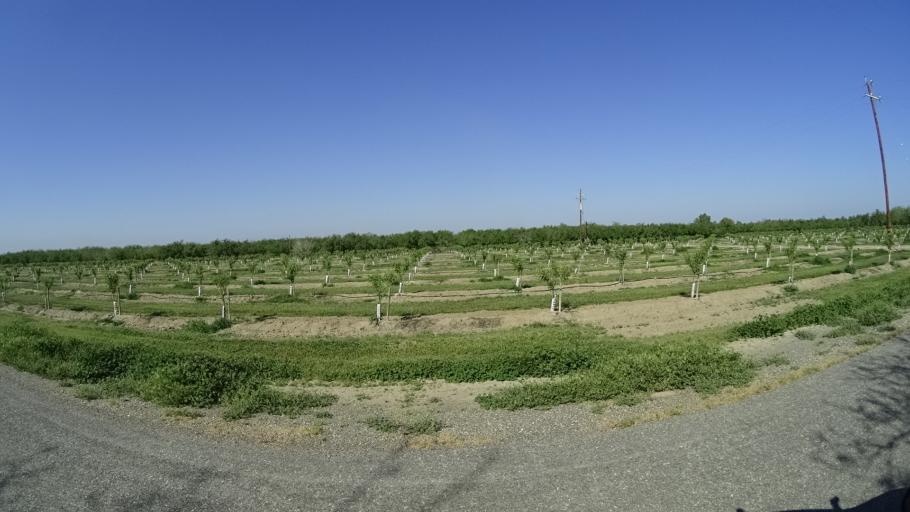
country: US
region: California
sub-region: Glenn County
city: Hamilton City
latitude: 39.6208
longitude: -122.0276
